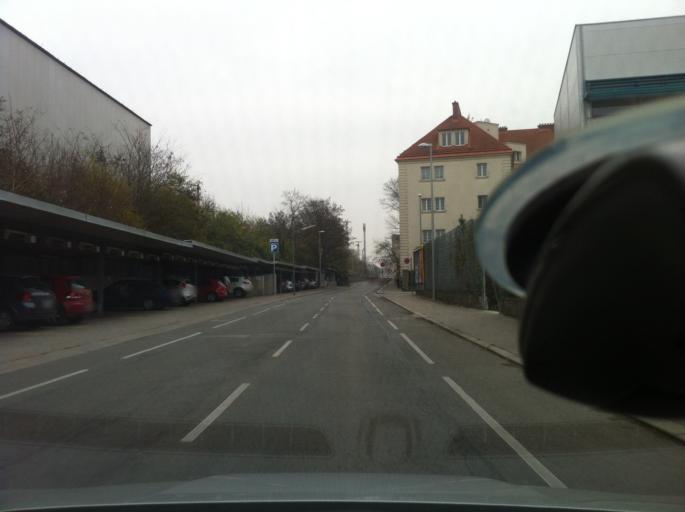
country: AT
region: Lower Austria
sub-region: Politischer Bezirk Modling
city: Perchtoldsdorf
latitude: 48.1924
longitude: 16.2899
